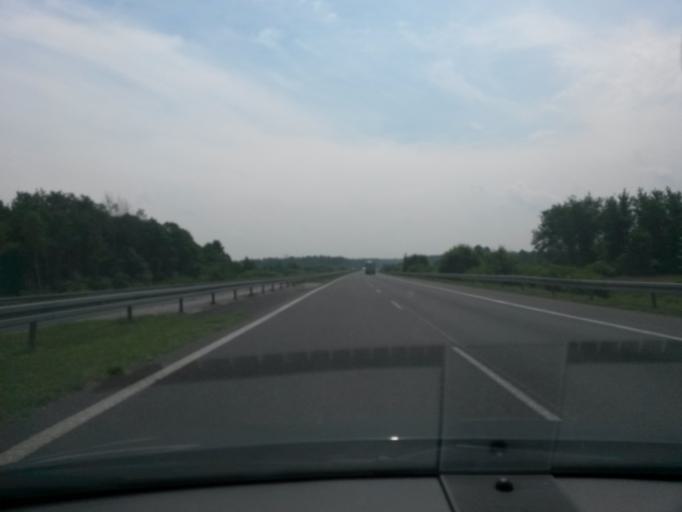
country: PL
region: Lodz Voivodeship
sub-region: Powiat radomszczanski
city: Kamiensk
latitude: 51.2561
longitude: 19.5279
